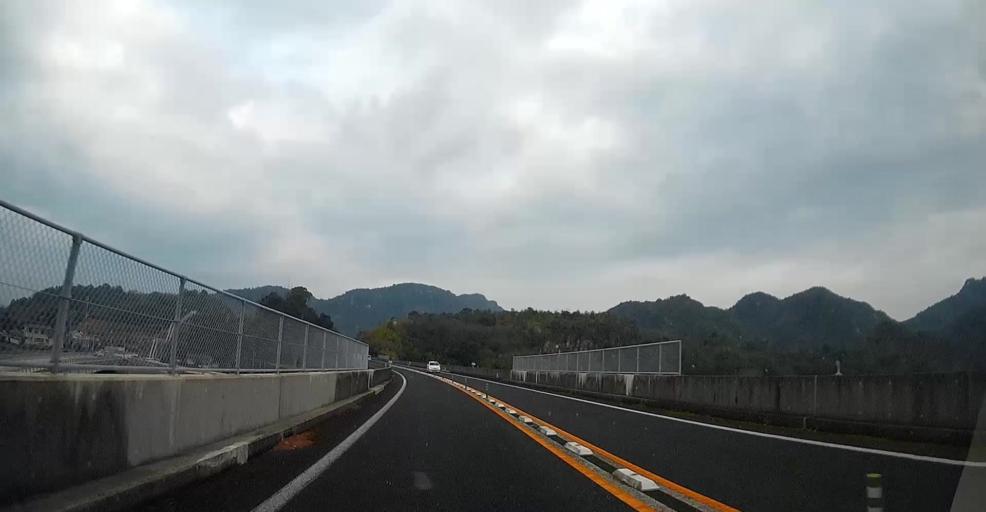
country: JP
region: Kumamoto
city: Hondo
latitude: 32.4974
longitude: 130.3942
